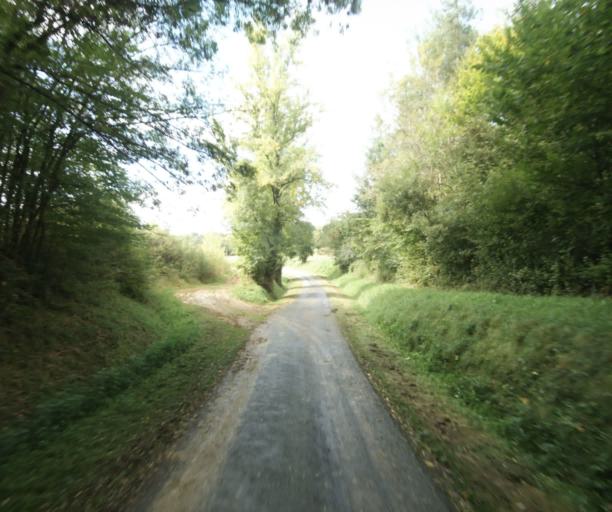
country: FR
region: Aquitaine
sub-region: Departement des Landes
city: Villeneuve-de-Marsan
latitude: 43.8972
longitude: -0.2071
